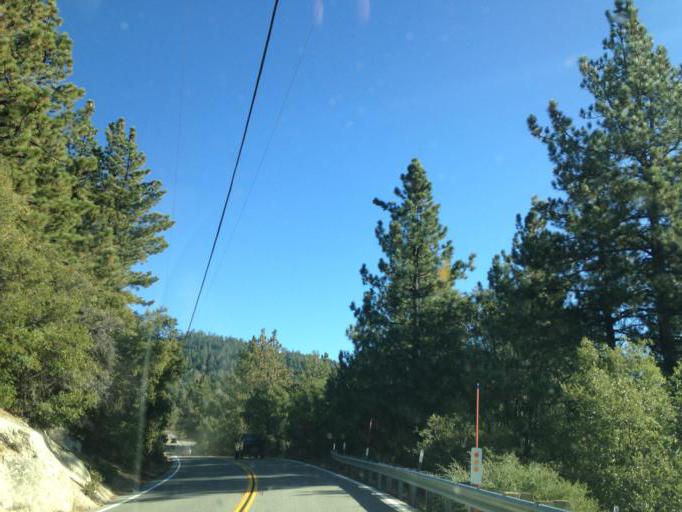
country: US
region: California
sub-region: Riverside County
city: Idyllwild-Pine Cove
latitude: 33.7807
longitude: -116.7472
